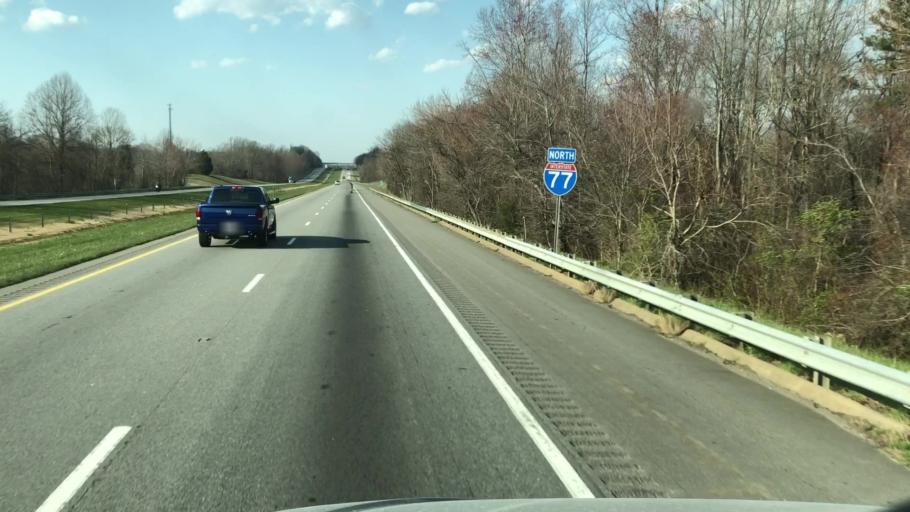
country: US
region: North Carolina
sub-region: Yadkin County
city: Yadkinville
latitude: 36.0568
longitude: -80.8225
